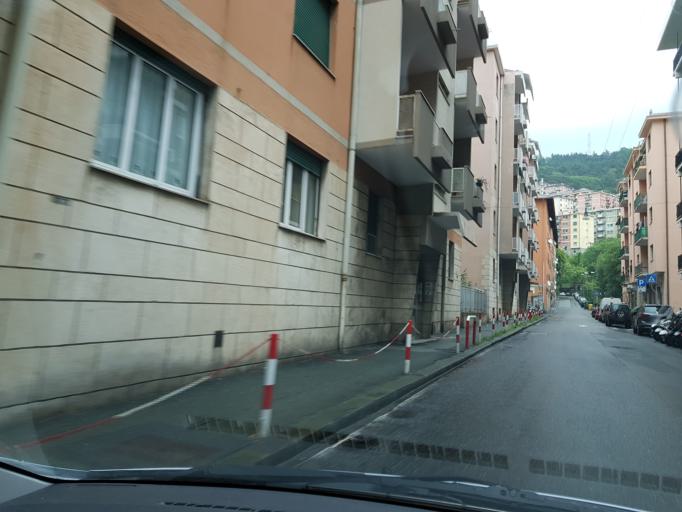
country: IT
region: Liguria
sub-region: Provincia di Genova
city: Genoa
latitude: 44.4247
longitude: 8.9263
